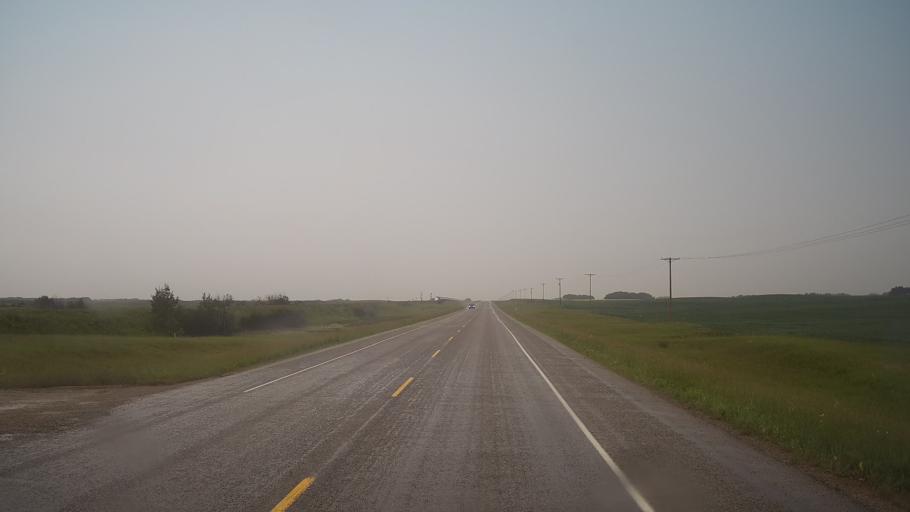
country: CA
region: Saskatchewan
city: Biggar
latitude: 52.1552
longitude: -108.2529
